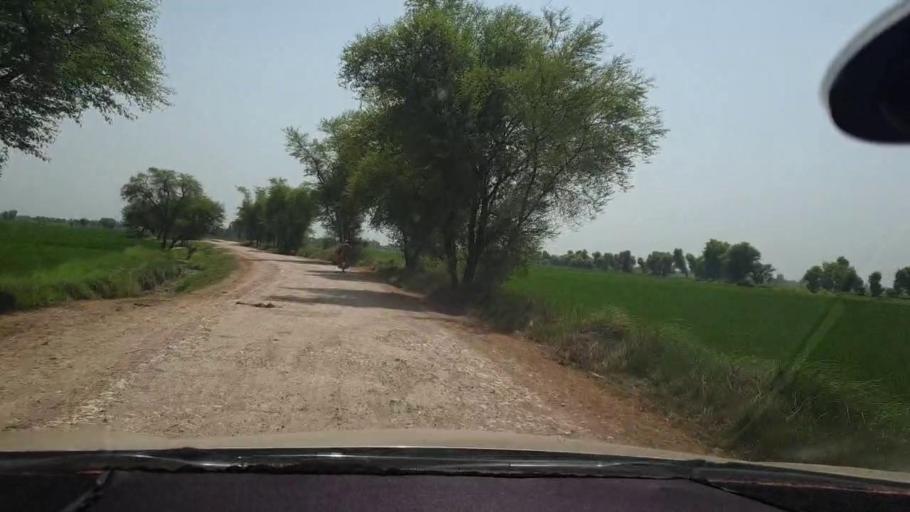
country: PK
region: Sindh
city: Kambar
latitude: 27.6827
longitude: 67.9384
